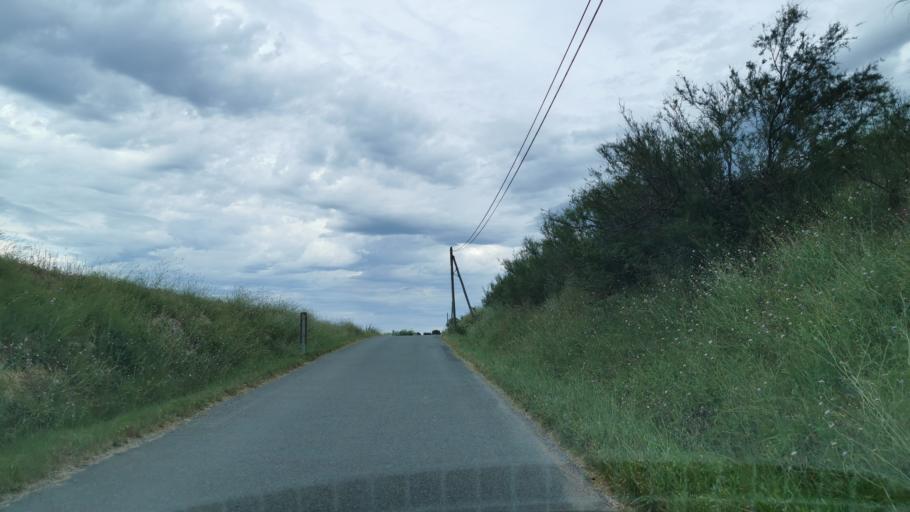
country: FR
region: Languedoc-Roussillon
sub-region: Departement de l'Aude
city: Moussan
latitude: 43.2375
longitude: 2.9603
